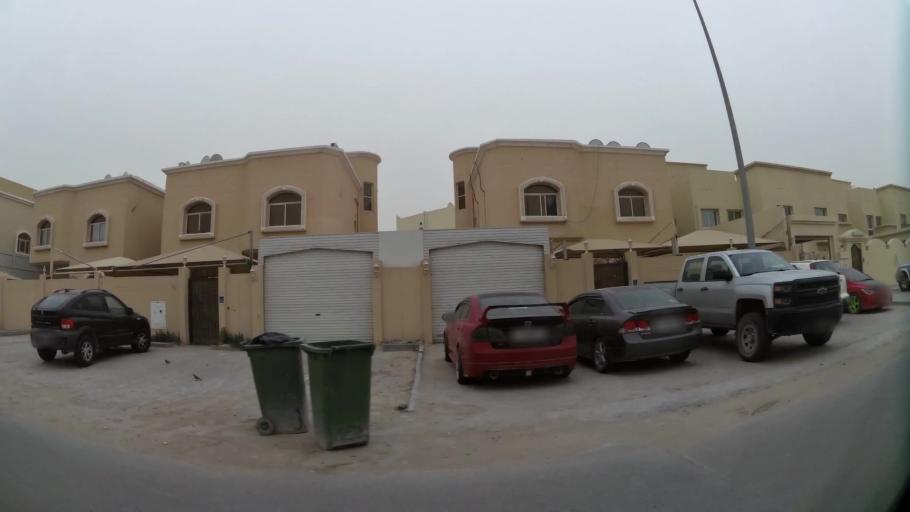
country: QA
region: Baladiyat ad Dawhah
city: Doha
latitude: 25.2436
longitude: 51.4879
